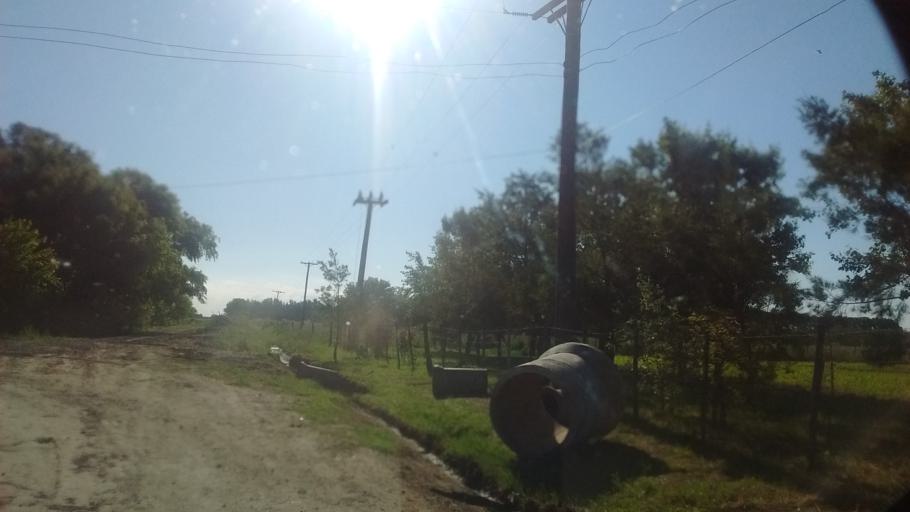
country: AR
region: Santa Fe
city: Funes
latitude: -32.8610
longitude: -60.8029
